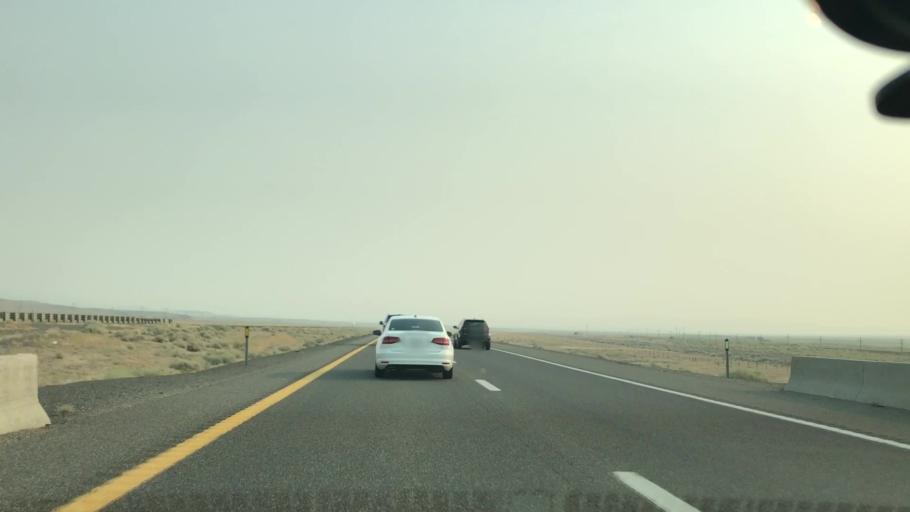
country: US
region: Nevada
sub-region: Pershing County
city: Lovelock
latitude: 40.0111
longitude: -118.6772
